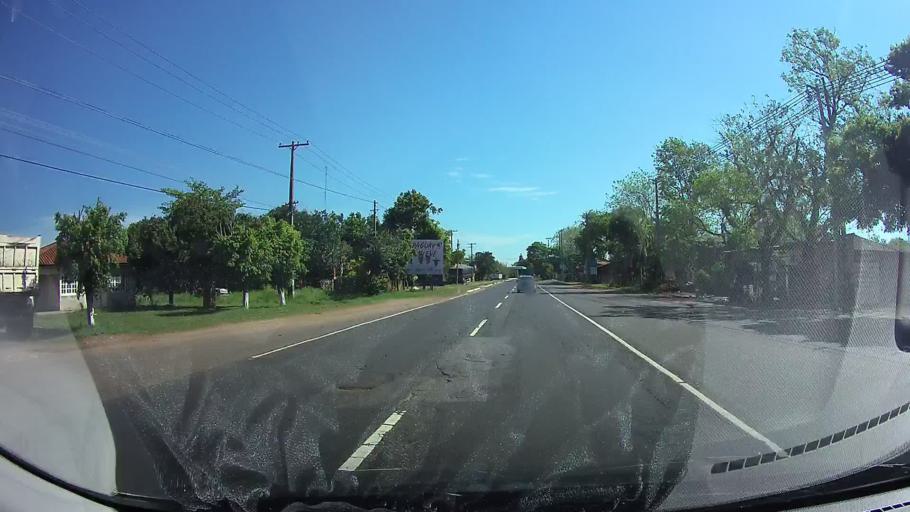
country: PY
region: Central
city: Ypacarai
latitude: -25.3963
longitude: -57.2811
